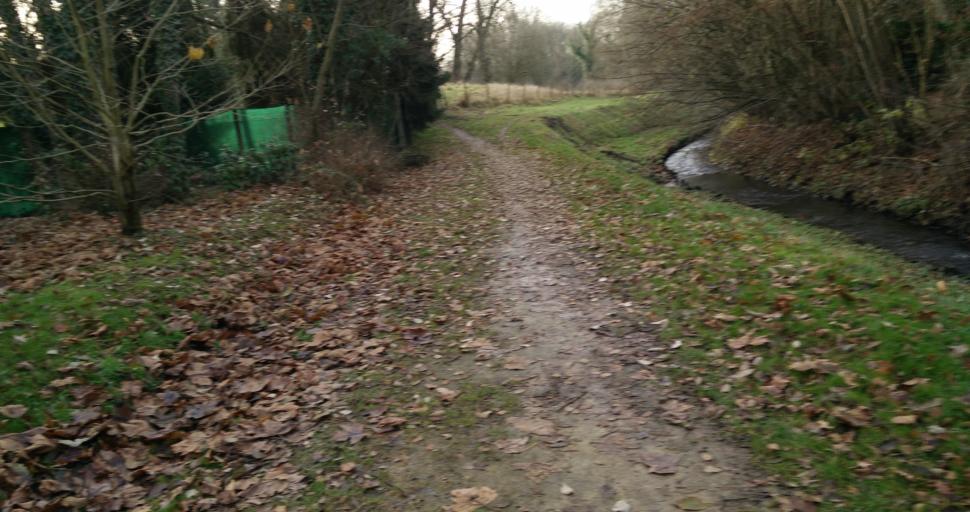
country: BE
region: Flanders
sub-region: Provincie Vlaams-Brabant
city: Sint-Genesius-Rode
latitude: 50.7380
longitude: 4.3289
